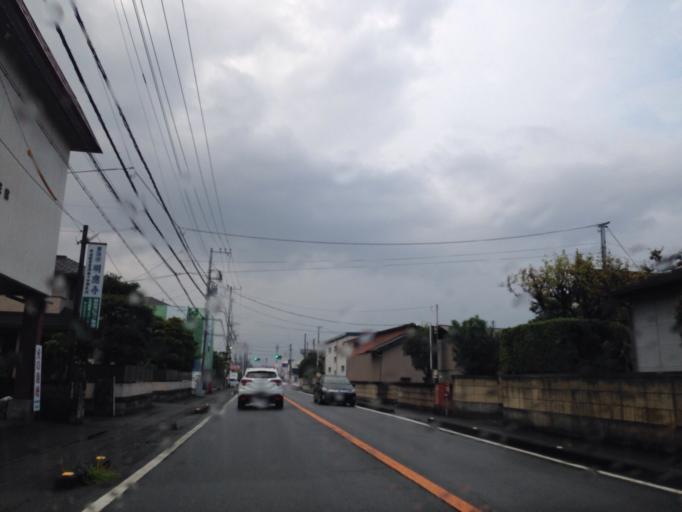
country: JP
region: Shizuoka
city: Mishima
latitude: 35.0692
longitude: 138.9422
